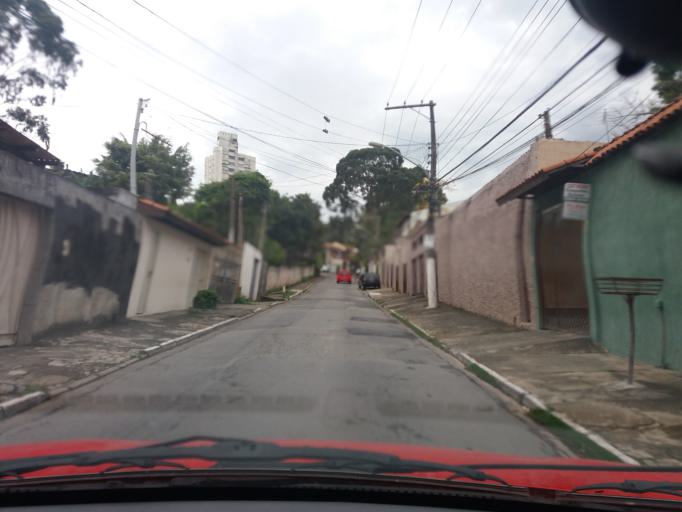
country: BR
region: Sao Paulo
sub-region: Taboao Da Serra
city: Taboao da Serra
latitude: -23.6177
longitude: -46.7485
